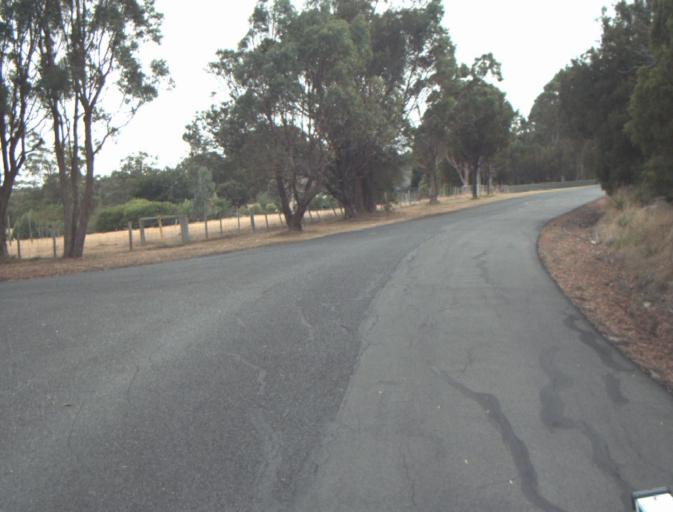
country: AU
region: Tasmania
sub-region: Launceston
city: Mayfield
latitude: -41.3289
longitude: 147.0588
